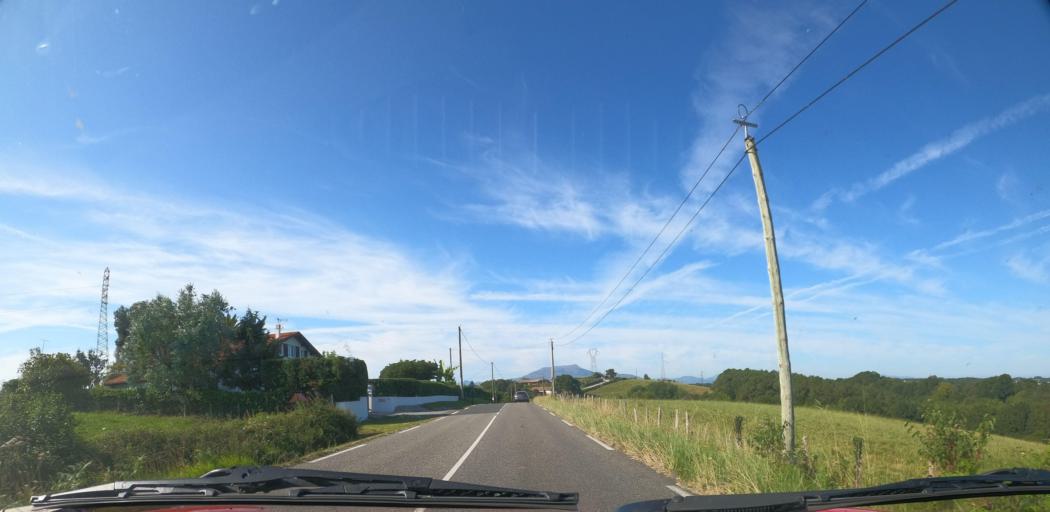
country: FR
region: Aquitaine
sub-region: Departement des Pyrenees-Atlantiques
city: Arcangues
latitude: 43.3961
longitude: -1.5318
